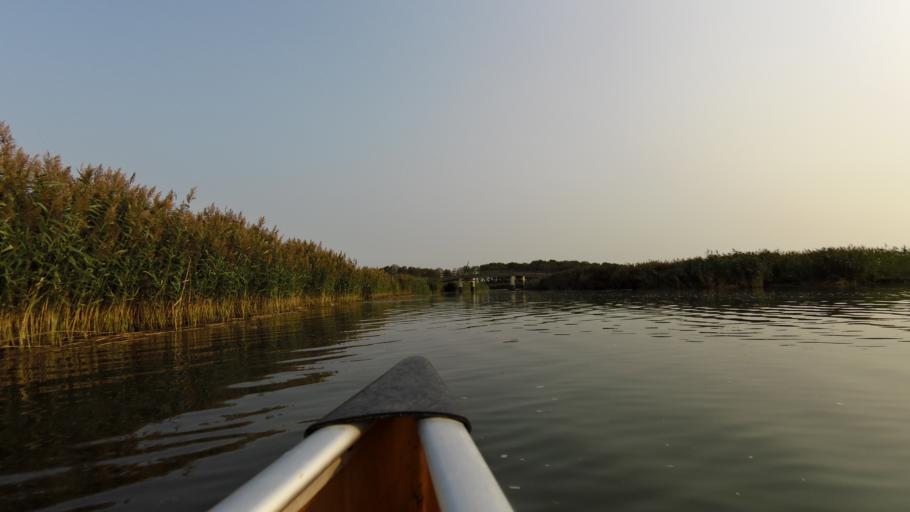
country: NL
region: South Holland
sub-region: Gemeente Sliedrecht
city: Sliedrecht
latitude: 51.7800
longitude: 4.8172
